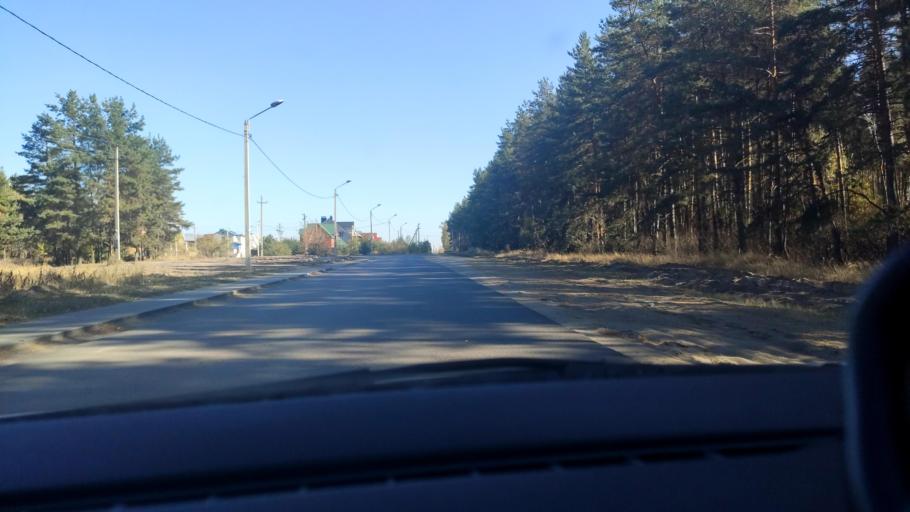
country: RU
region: Voronezj
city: Pridonskoy
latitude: 51.6259
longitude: 39.0861
